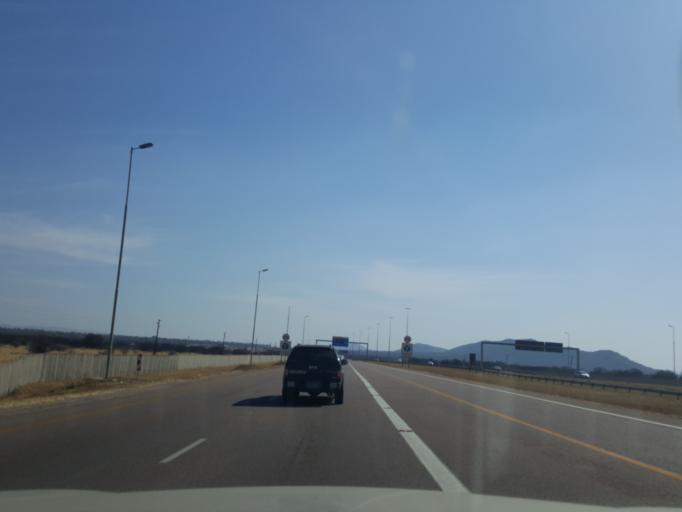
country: ZA
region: Gauteng
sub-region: City of Tshwane Metropolitan Municipality
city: Pretoria
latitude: -25.6445
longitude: 28.2679
